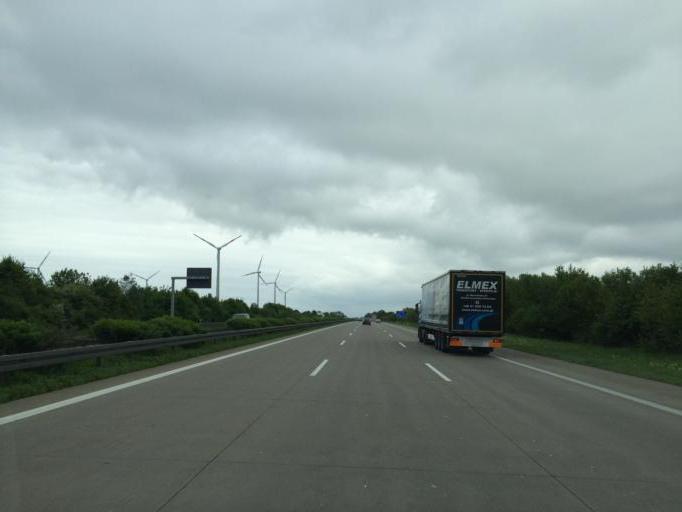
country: DE
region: Saxony-Anhalt
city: Eichenbarleben
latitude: 52.1871
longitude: 11.3752
